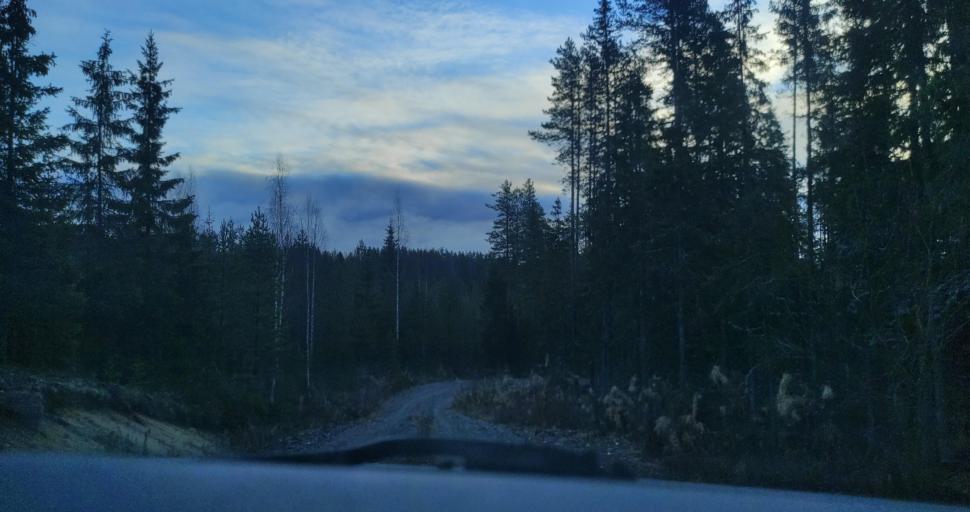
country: RU
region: Republic of Karelia
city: Pitkyaranta
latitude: 61.7402
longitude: 31.3631
